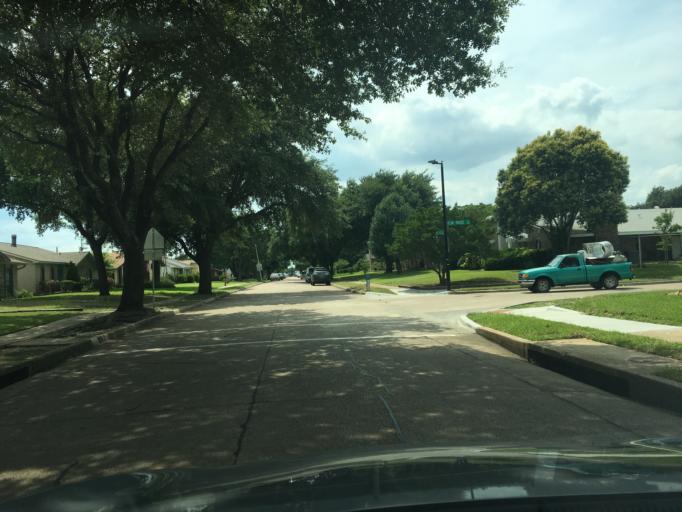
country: US
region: Texas
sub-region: Dallas County
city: Richardson
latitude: 32.9551
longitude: -96.6780
